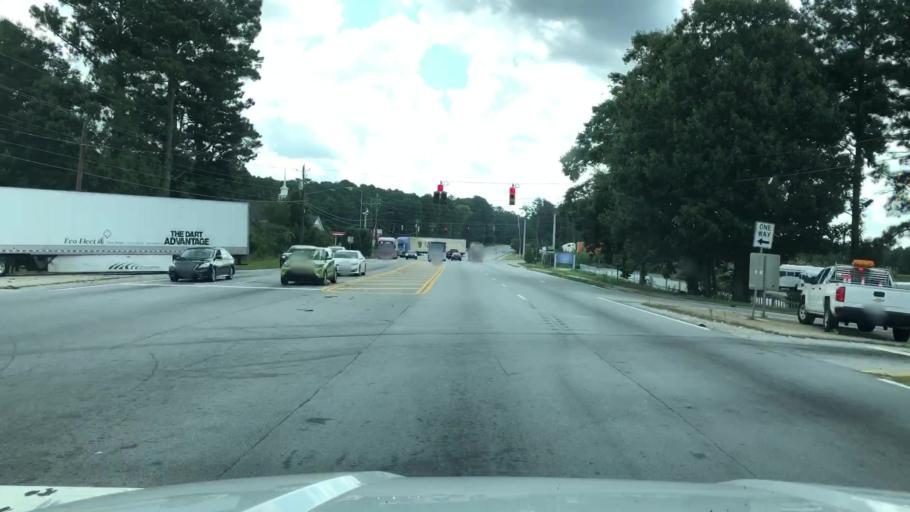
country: US
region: Georgia
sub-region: Fulton County
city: Union City
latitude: 33.5843
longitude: -84.5122
